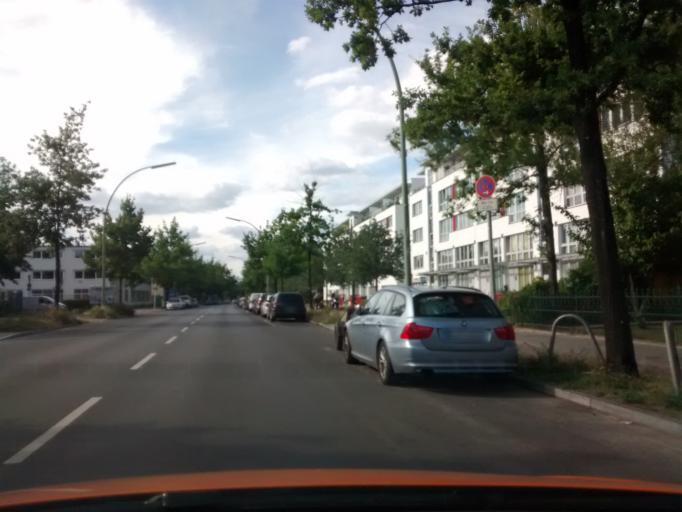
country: DE
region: Berlin
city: Marienfelde
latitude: 52.4174
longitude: 13.3607
